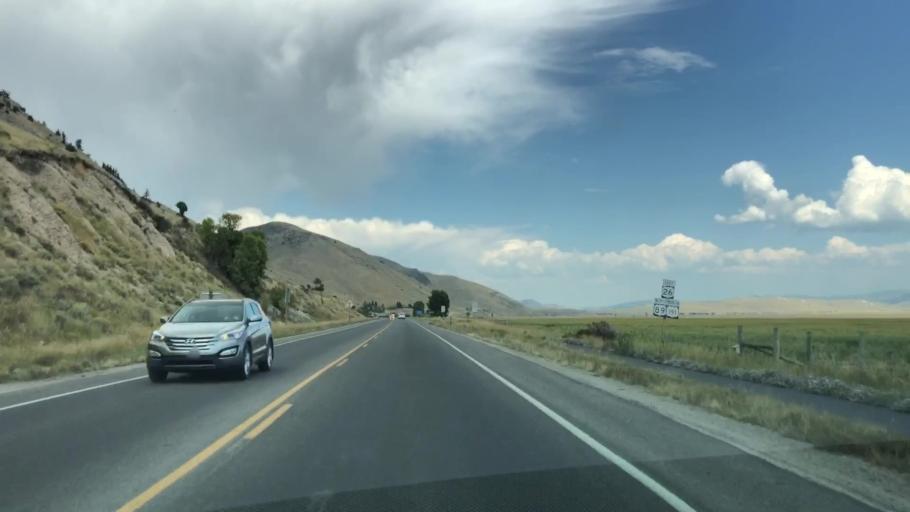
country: US
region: Wyoming
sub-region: Teton County
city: Jackson
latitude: 43.4915
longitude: -110.7616
